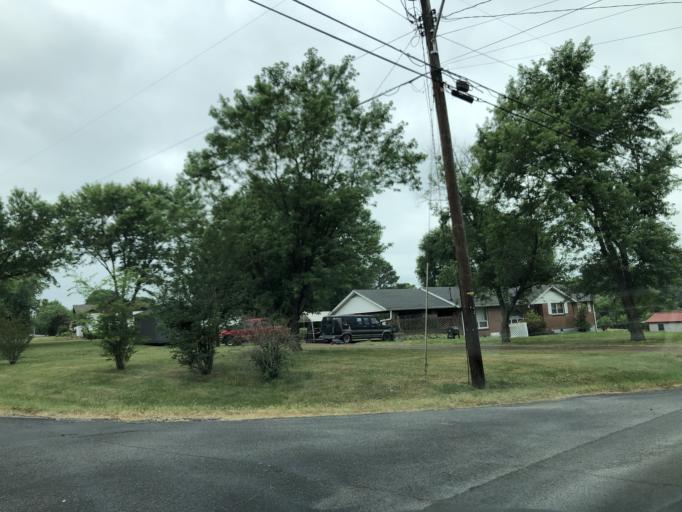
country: US
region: Tennessee
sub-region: Davidson County
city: Goodlettsville
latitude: 36.2810
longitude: -86.7199
